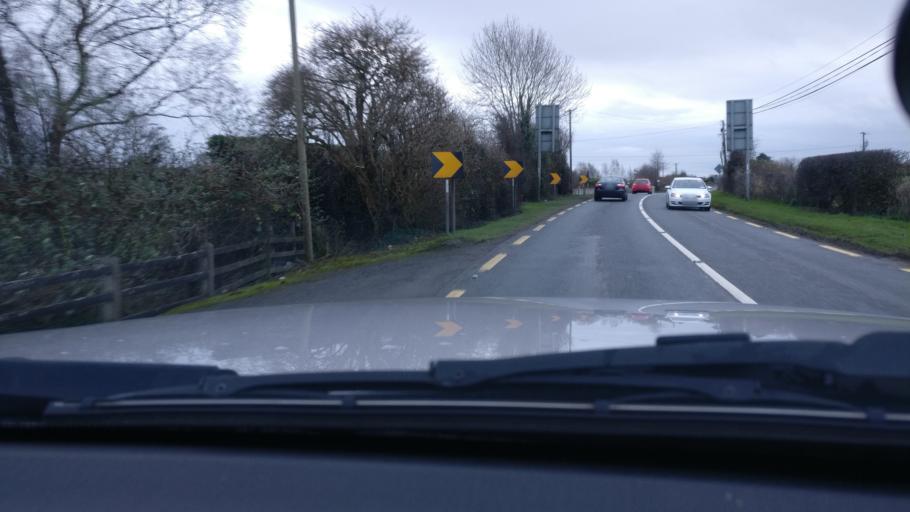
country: IE
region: Leinster
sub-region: An Iarmhi
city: Athlone
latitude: 53.4451
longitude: -7.8872
